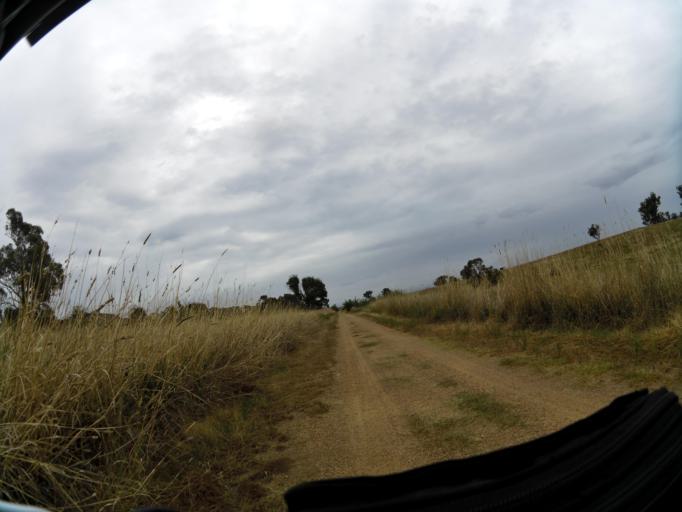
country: AU
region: New South Wales
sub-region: Albury Municipality
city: East Albury
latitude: -36.2074
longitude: 147.0526
